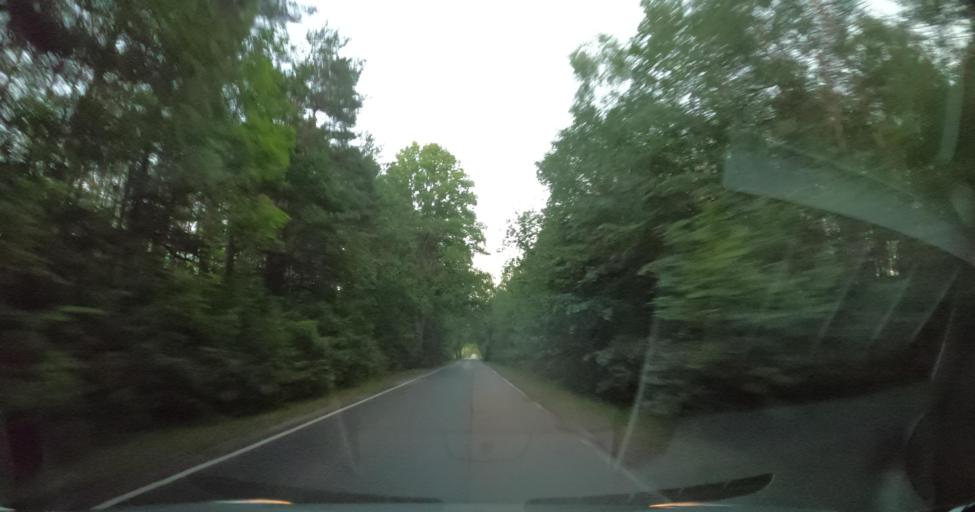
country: PL
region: Pomeranian Voivodeship
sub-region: Powiat wejherowski
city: Luzino
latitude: 54.4651
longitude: 18.1172
